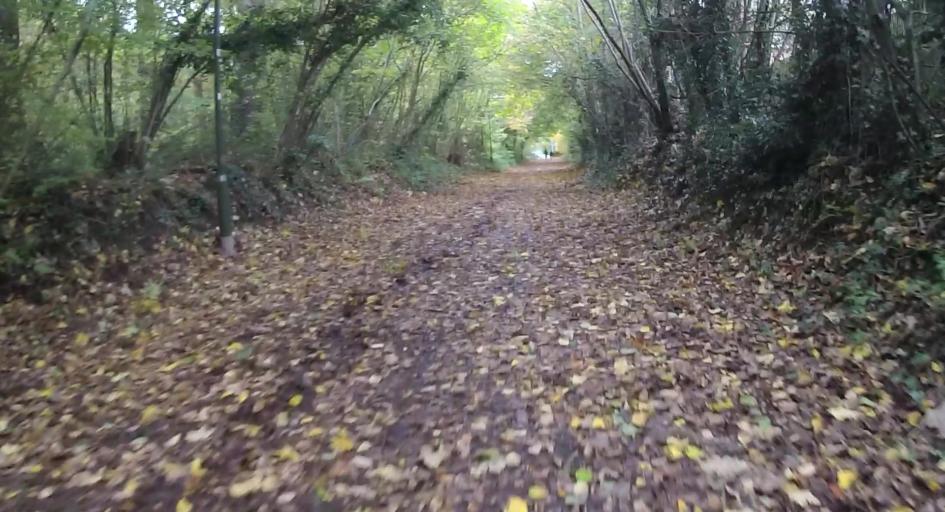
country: GB
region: England
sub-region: Hampshire
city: Old Basing
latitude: 51.2869
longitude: -1.0525
